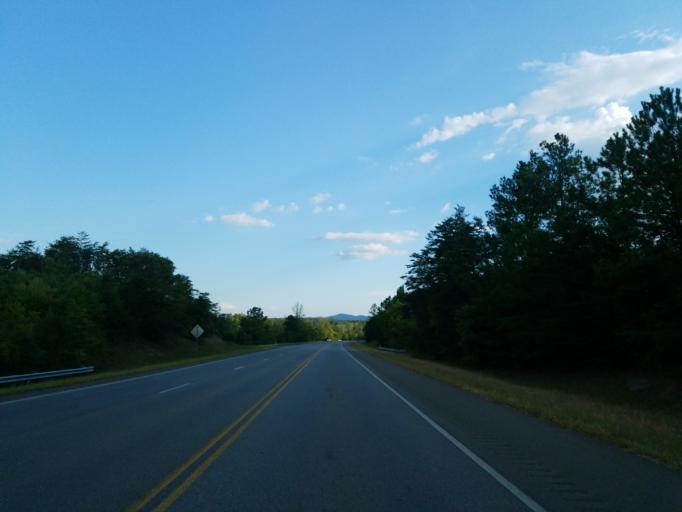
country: US
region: Georgia
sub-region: Murray County
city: Chatsworth
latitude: 34.6732
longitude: -84.7244
